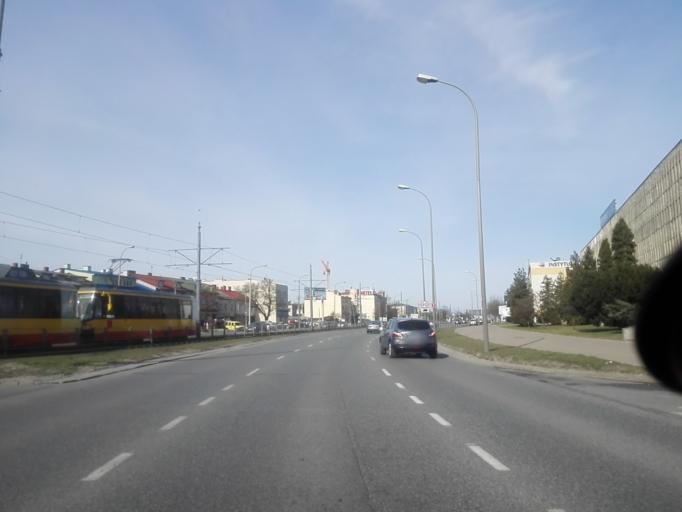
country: PL
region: Masovian Voivodeship
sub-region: Warszawa
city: Wlochy
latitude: 52.1766
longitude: 20.9450
